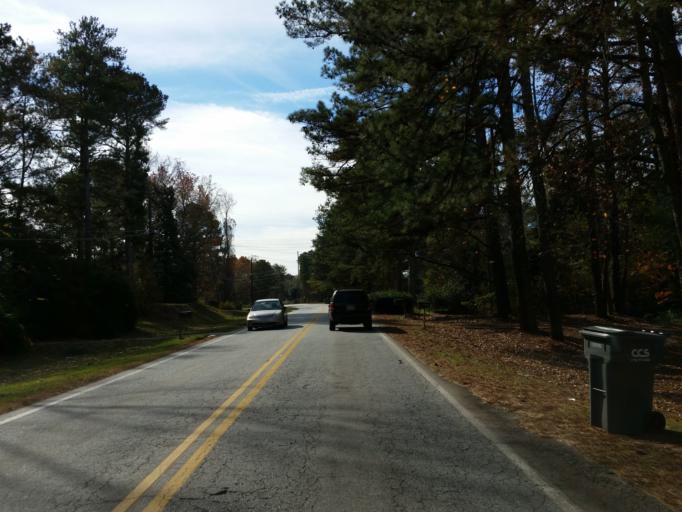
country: US
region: Georgia
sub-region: Douglas County
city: Lithia Springs
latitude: 33.7420
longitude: -84.6659
